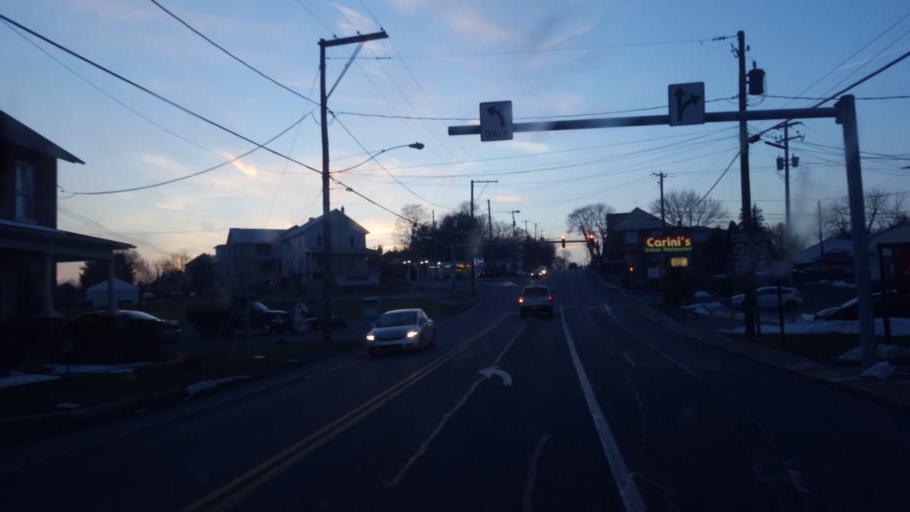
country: US
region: Pennsylvania
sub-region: Lancaster County
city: Blue Ball
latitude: 40.1181
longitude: -76.0471
